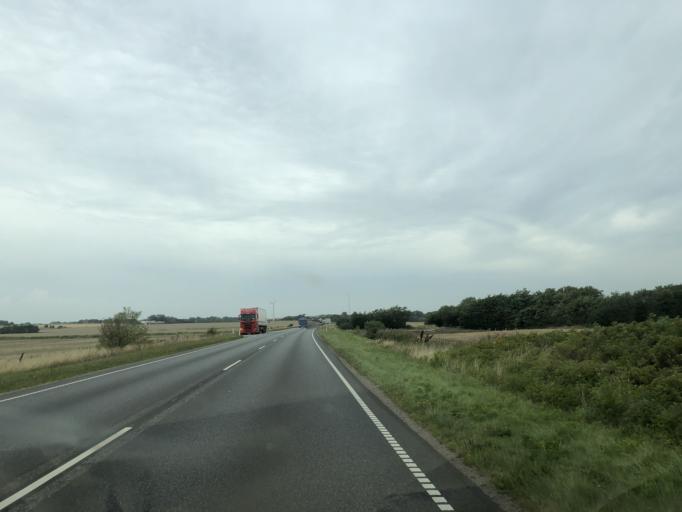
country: DK
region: North Denmark
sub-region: Morso Kommune
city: Nykobing Mors
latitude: 56.7784
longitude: 8.8208
